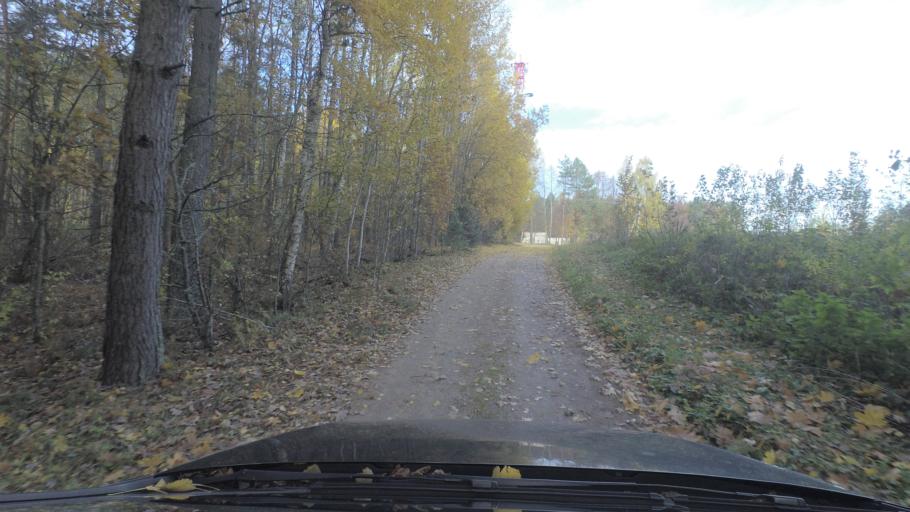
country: LT
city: Ignalina
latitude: 55.3365
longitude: 26.1768
